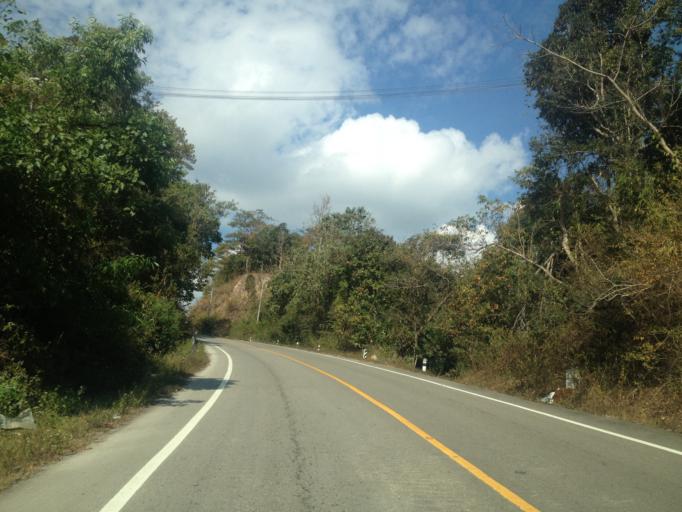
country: TH
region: Mae Hong Son
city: Ban Huai I Huak
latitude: 18.1402
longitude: 98.1725
